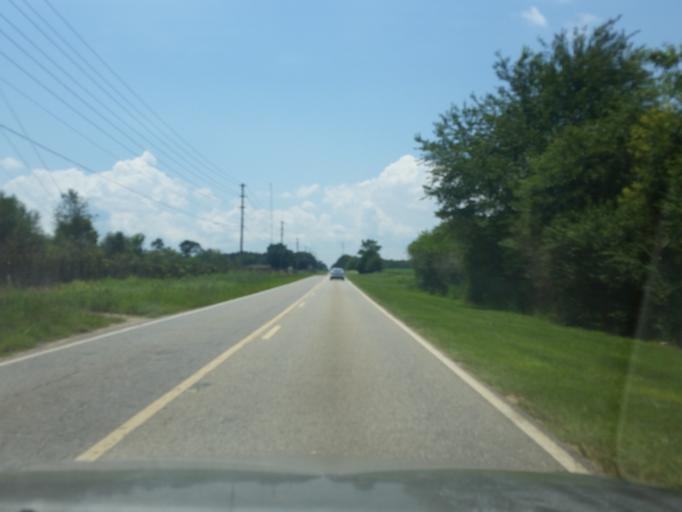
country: US
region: Alabama
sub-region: Baldwin County
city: Robertsdale
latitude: 30.6261
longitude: -87.6348
